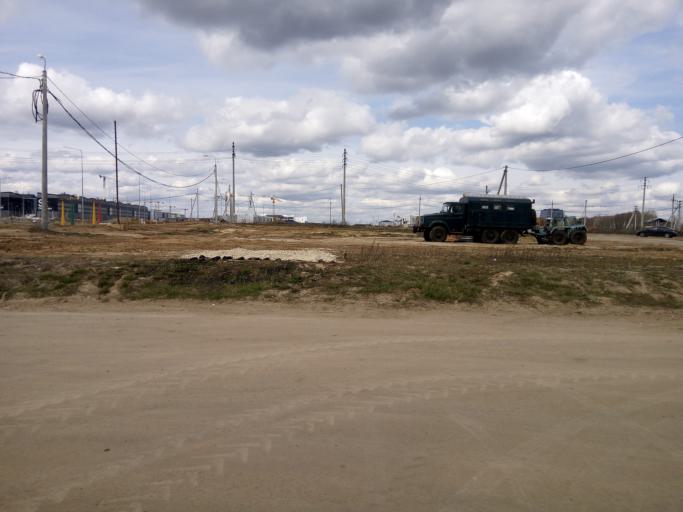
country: RU
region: Moskovskaya
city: Skolkovo
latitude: 55.6858
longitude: 37.3535
